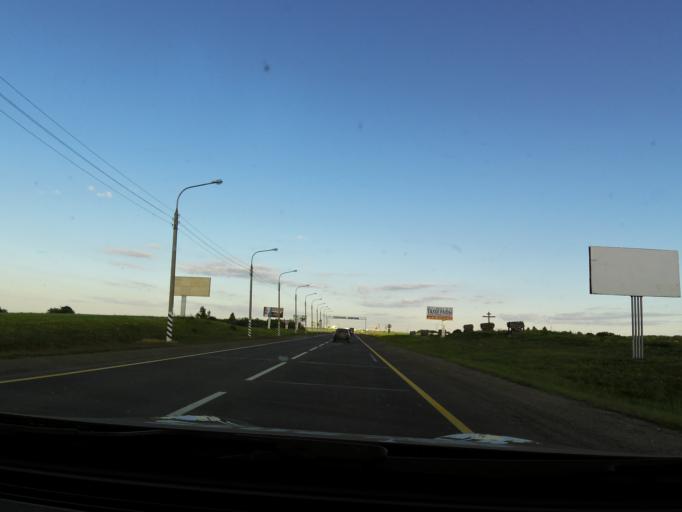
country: RU
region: Vologda
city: Vologda
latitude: 59.1694
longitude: 39.9117
